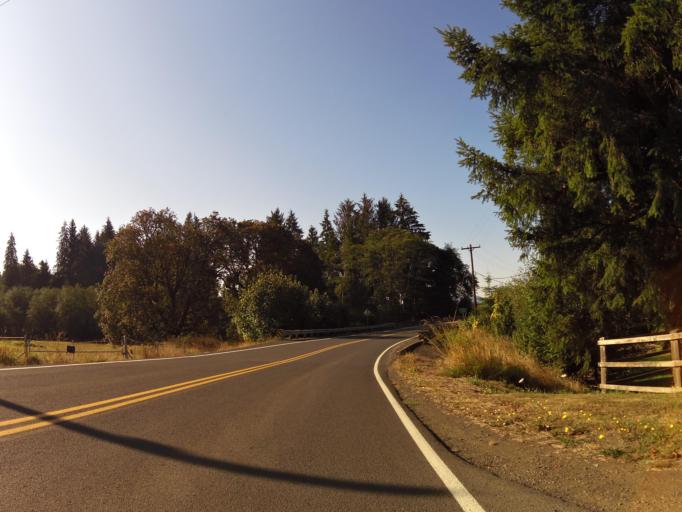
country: US
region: Oregon
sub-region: Tillamook County
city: Tillamook
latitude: 45.3866
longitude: -123.7949
